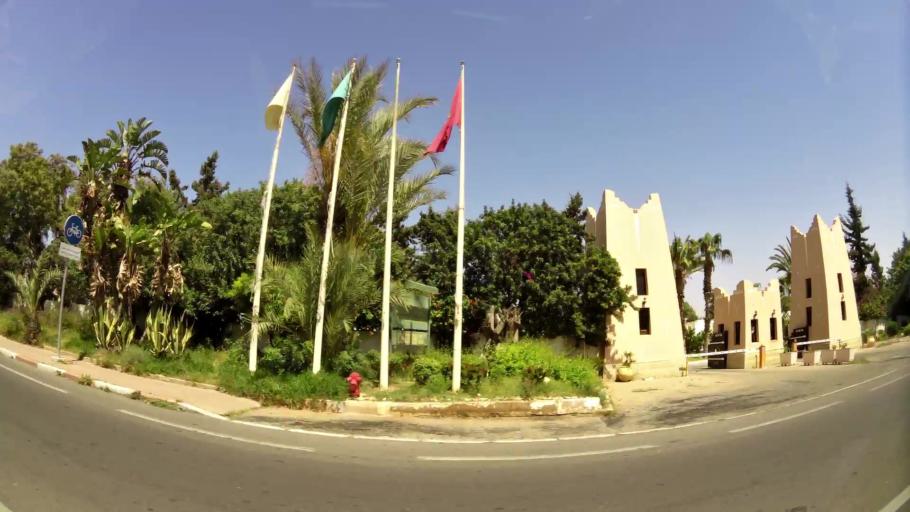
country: MA
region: Souss-Massa-Draa
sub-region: Agadir-Ida-ou-Tnan
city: Agadir
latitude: 30.4354
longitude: -9.5958
